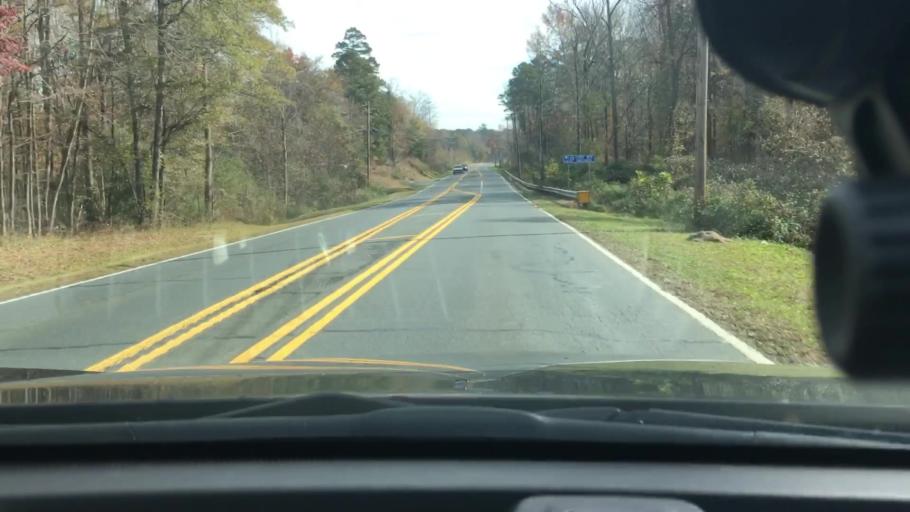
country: US
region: North Carolina
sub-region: Stanly County
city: Badin
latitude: 35.3176
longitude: -80.1132
